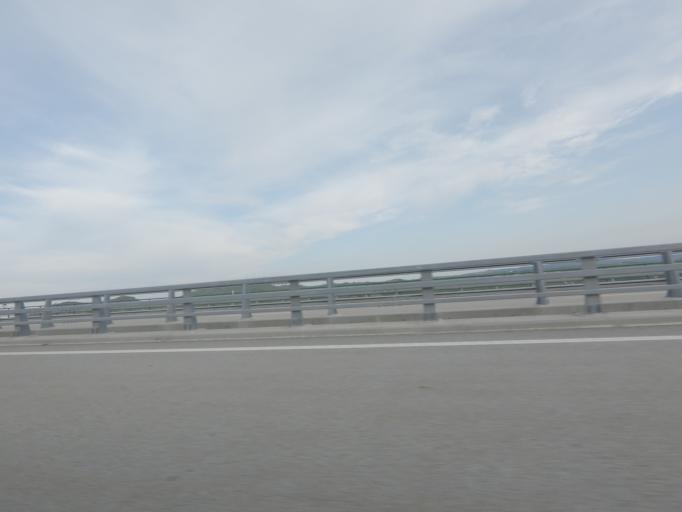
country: PT
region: Vila Real
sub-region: Vila Pouca de Aguiar
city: Vila Pouca de Aguiar
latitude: 41.3861
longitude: -7.6581
